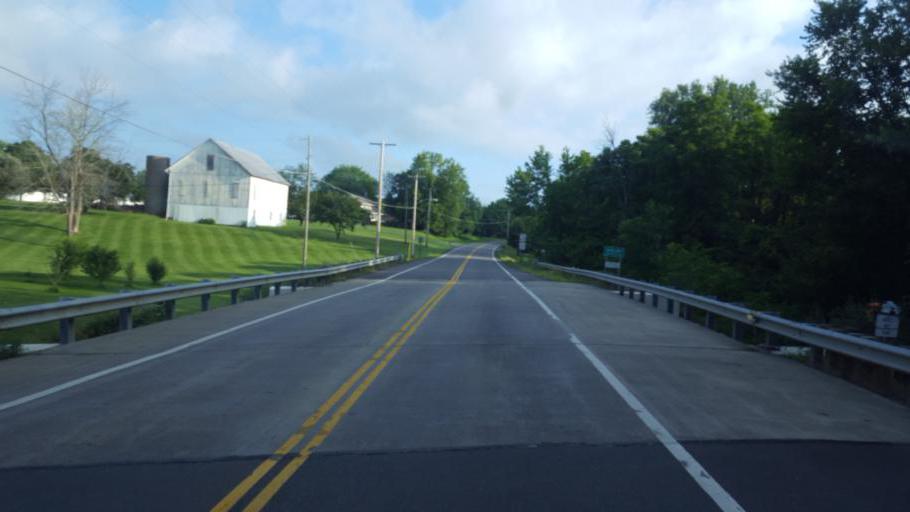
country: US
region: Ohio
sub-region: Richland County
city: Shelby
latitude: 40.8636
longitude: -82.6633
